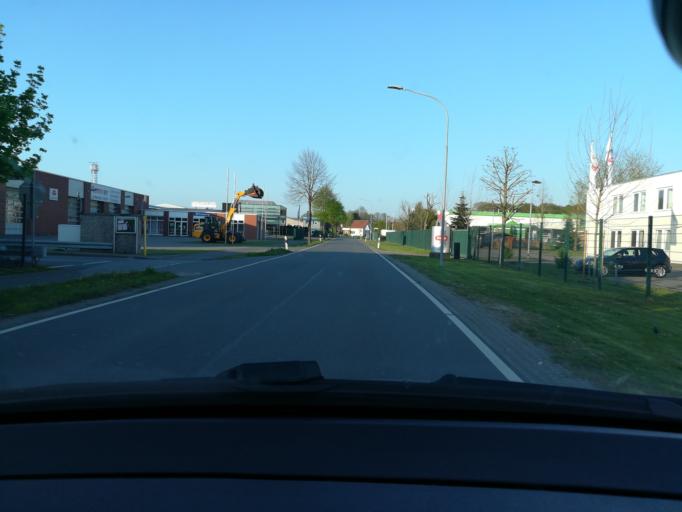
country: DE
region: Lower Saxony
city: Dissen
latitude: 52.0702
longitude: 8.1961
